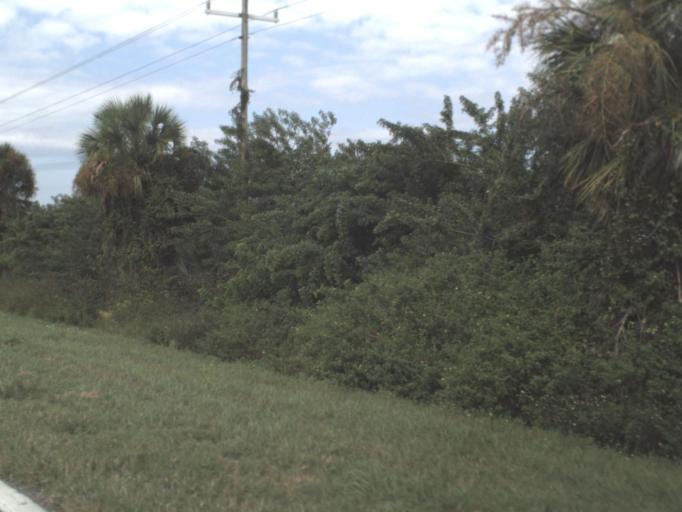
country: US
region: Florida
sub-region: Glades County
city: Moore Haven
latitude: 26.7684
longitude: -81.1996
